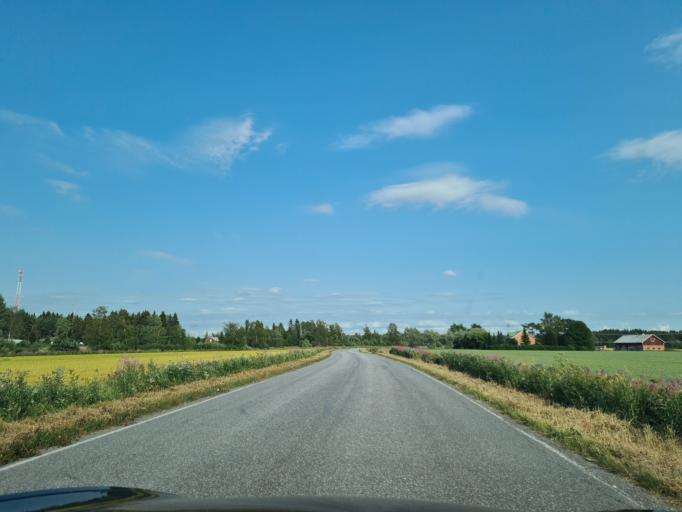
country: FI
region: Ostrobothnia
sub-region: Vaasa
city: Ristinummi
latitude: 63.0300
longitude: 21.8253
